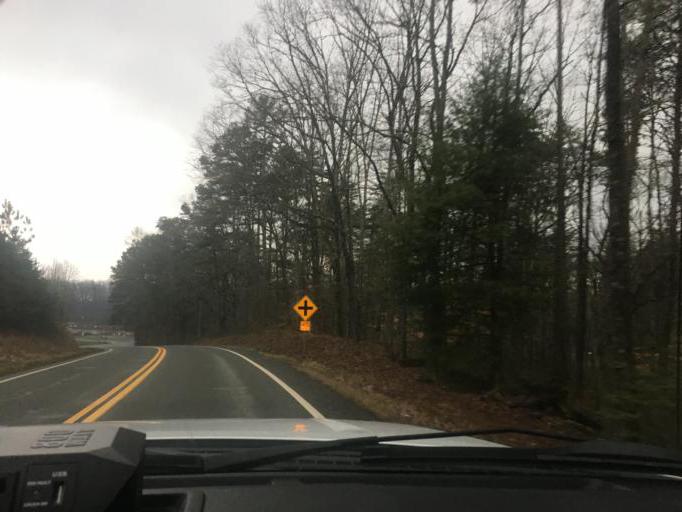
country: US
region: Georgia
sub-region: Dawson County
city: Dawsonville
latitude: 34.4261
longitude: -84.2321
